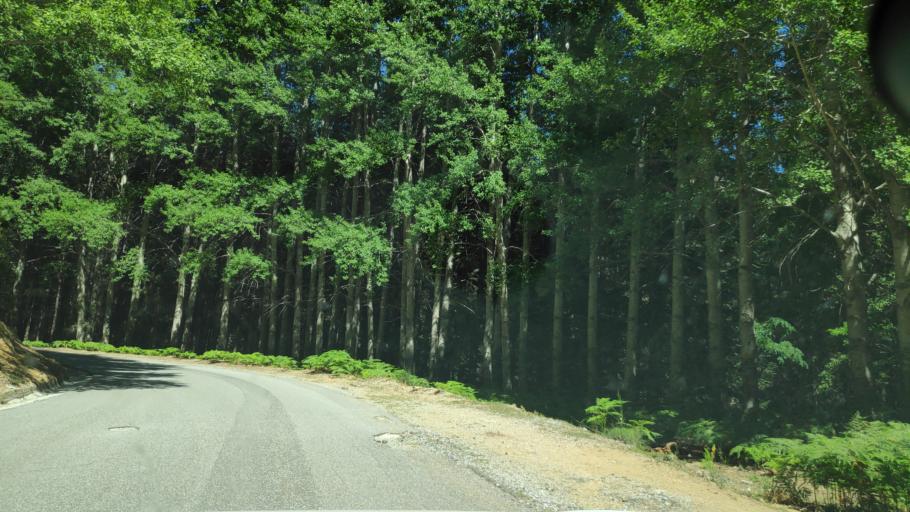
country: IT
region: Calabria
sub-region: Provincia di Reggio Calabria
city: Bova
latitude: 38.0352
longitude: 15.9501
